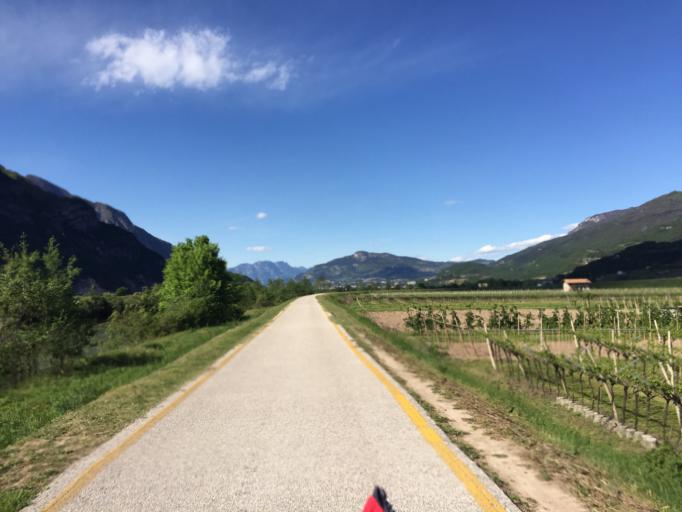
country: IT
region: Trentino-Alto Adige
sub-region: Provincia di Trento
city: Aldeno
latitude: 45.9792
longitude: 11.1102
